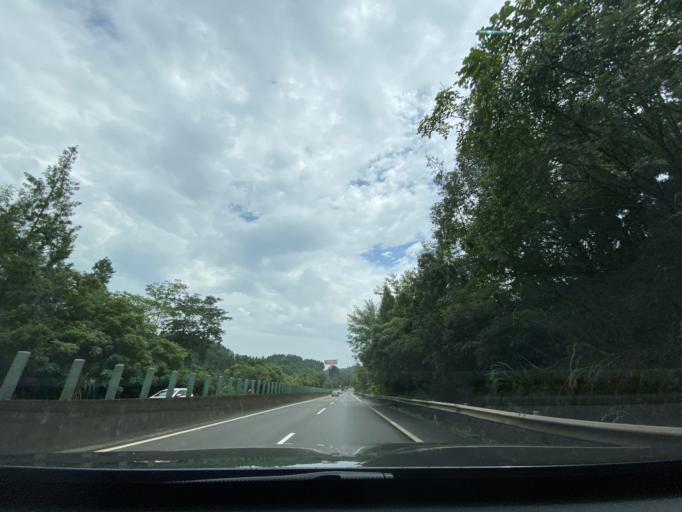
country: CN
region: Sichuan
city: Jiancheng
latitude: 30.3252
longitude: 104.5706
